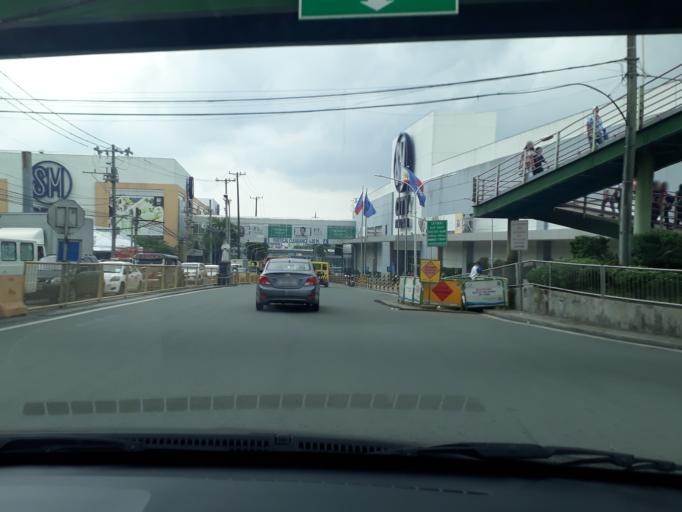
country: PH
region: Calabarzon
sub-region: Province of Rizal
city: Taguig
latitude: 14.4867
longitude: 121.0445
